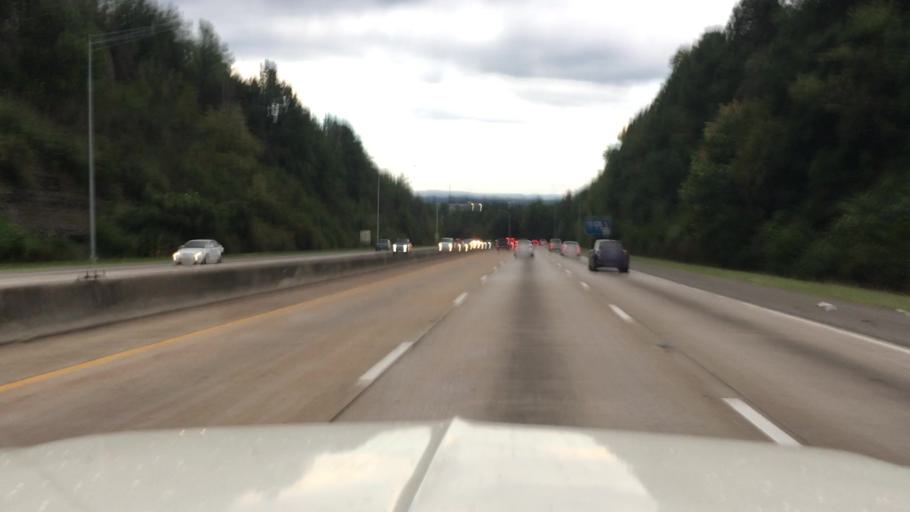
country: US
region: Alabama
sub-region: Jefferson County
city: Hoover
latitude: 33.4189
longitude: -86.8130
